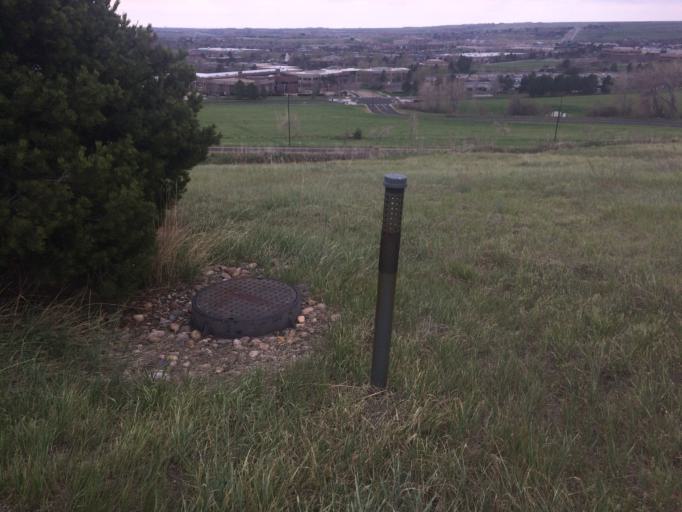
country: US
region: Colorado
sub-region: Boulder County
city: Superior
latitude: 39.9716
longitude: -105.1709
